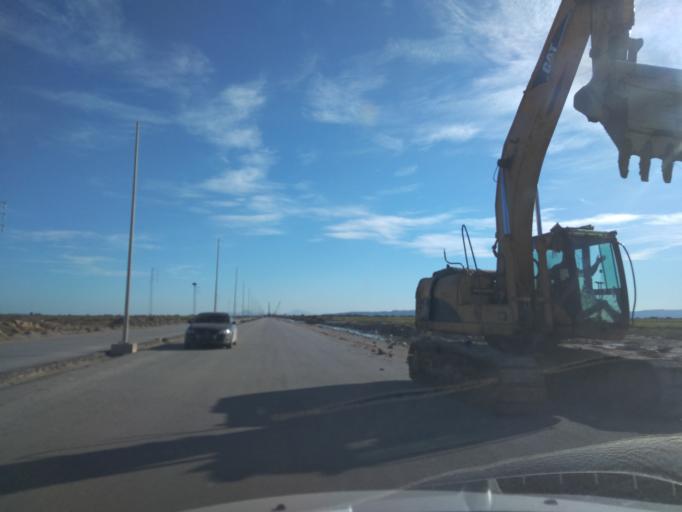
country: TN
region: Ariana
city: Qal'at al Andalus
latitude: 37.0318
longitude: 10.1359
